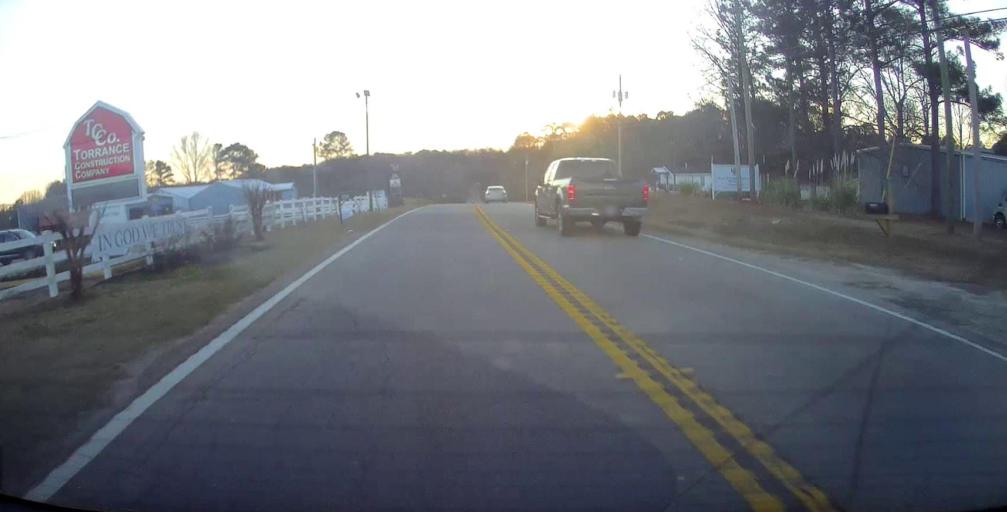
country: US
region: Georgia
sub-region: Troup County
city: La Grange
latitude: 33.0596
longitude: -84.9737
